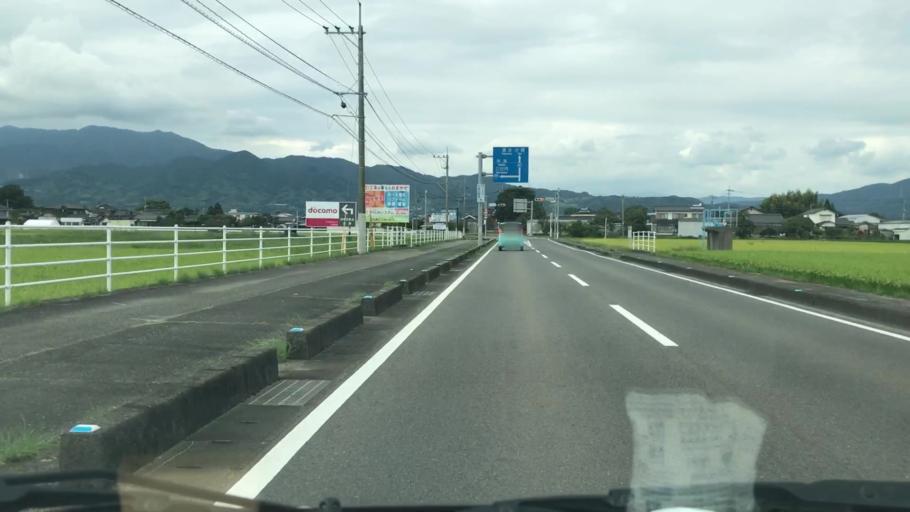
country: JP
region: Saga Prefecture
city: Saga-shi
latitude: 33.2833
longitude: 130.2519
